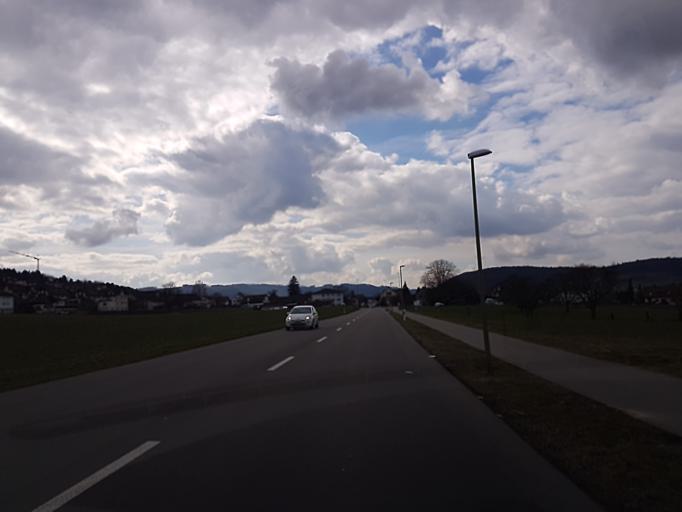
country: CH
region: Zurich
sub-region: Bezirk Dielsdorf
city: Daenikon
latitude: 47.4462
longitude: 8.3923
